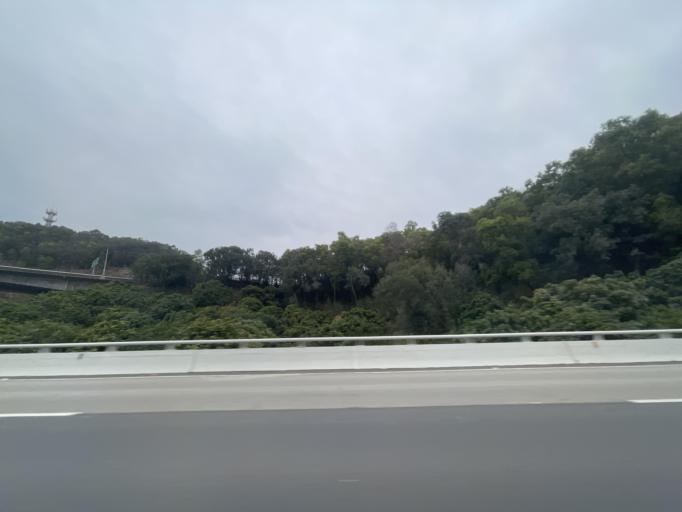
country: CN
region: Guangdong
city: Humen
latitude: 22.8075
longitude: 113.6419
